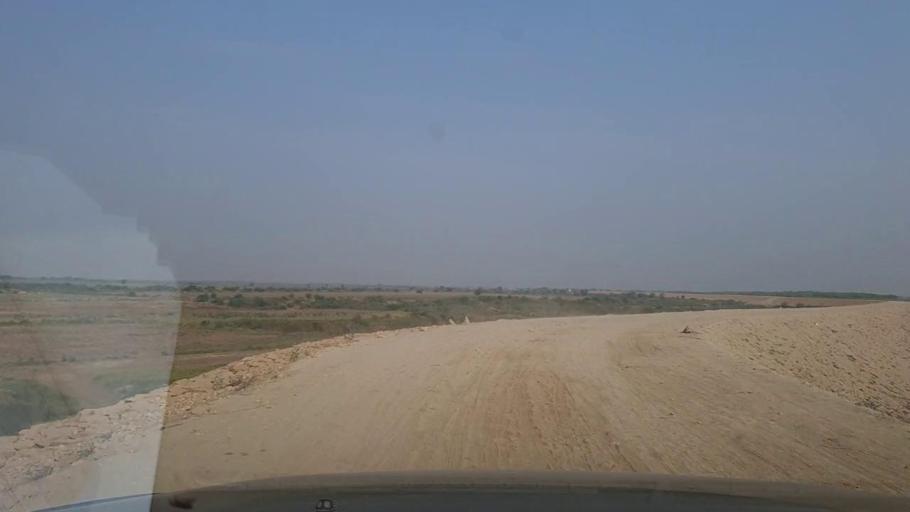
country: PK
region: Sindh
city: Bulri
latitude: 24.9570
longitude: 68.2908
